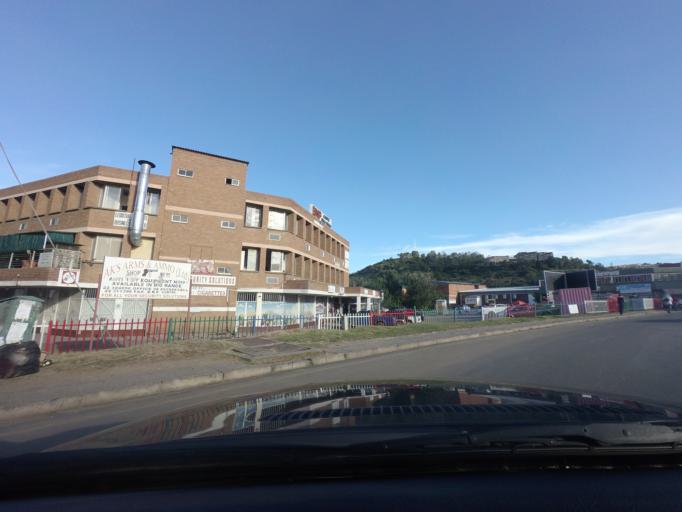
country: LS
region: Maseru
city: Maseru
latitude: -29.3139
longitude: 27.4873
